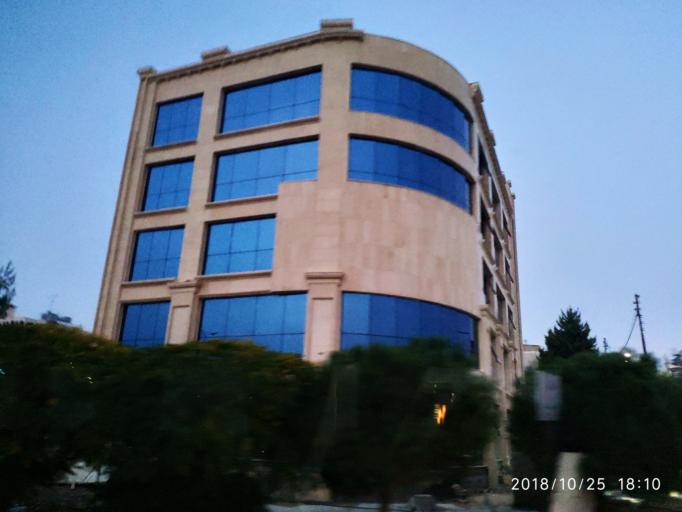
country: JO
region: Amman
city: Wadi as Sir
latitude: 31.9841
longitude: 35.8324
